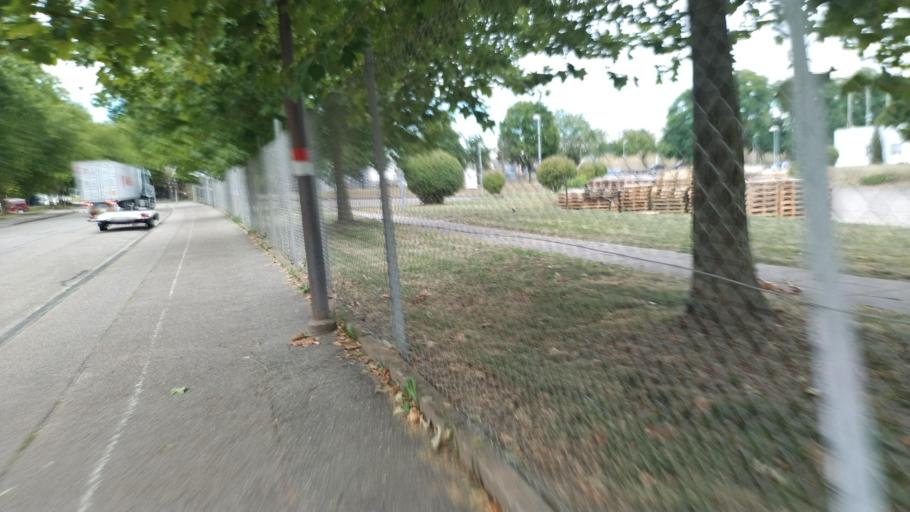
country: DE
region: Baden-Wuerttemberg
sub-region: Karlsruhe Region
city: Ettlingen
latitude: 48.9439
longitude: 8.3819
